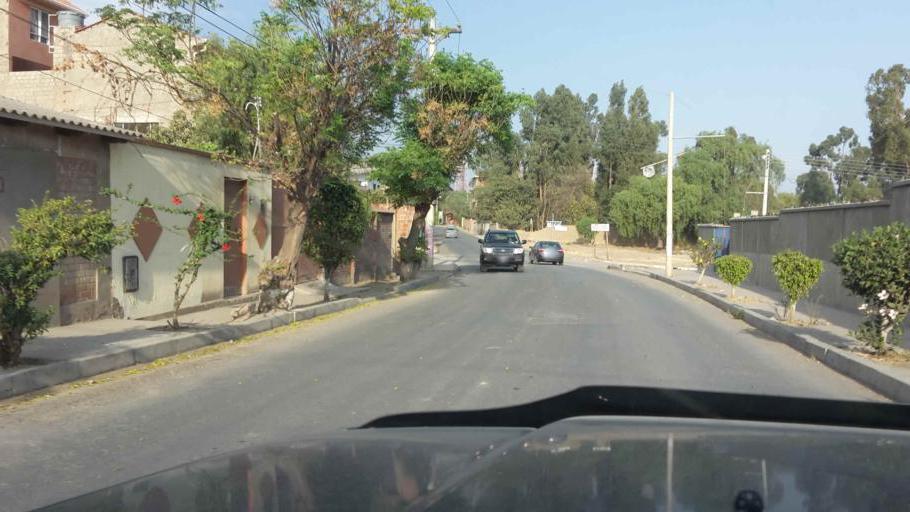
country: BO
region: Cochabamba
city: Cochabamba
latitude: -17.3412
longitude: -66.2162
